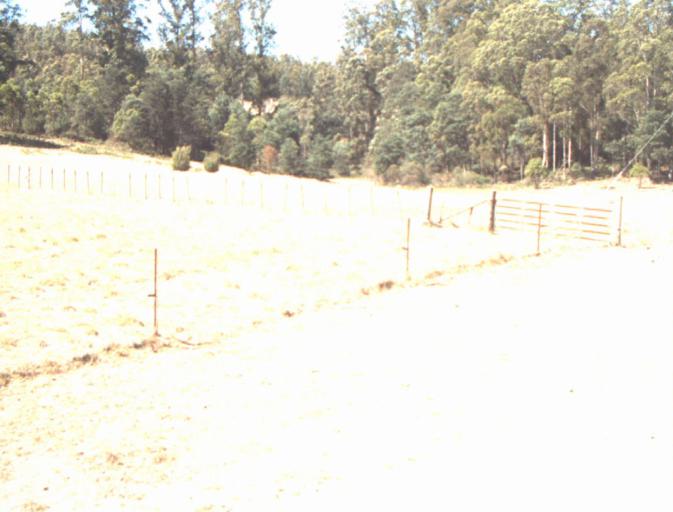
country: AU
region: Tasmania
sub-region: Dorset
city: Scottsdale
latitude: -41.2888
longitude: 147.3410
